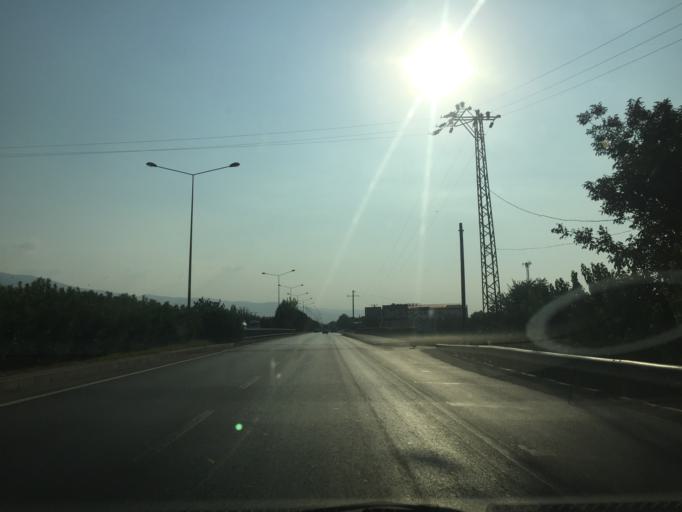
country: TR
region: Manisa
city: Salihli
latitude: 38.4921
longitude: 28.1684
